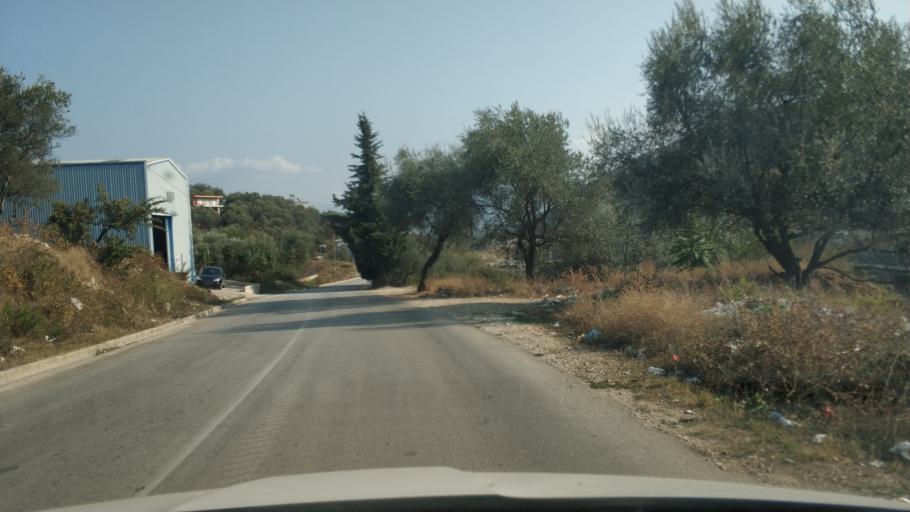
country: AL
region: Vlore
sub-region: Rrethi i Sarandes
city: Sarande
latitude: 39.8731
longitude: 20.0300
